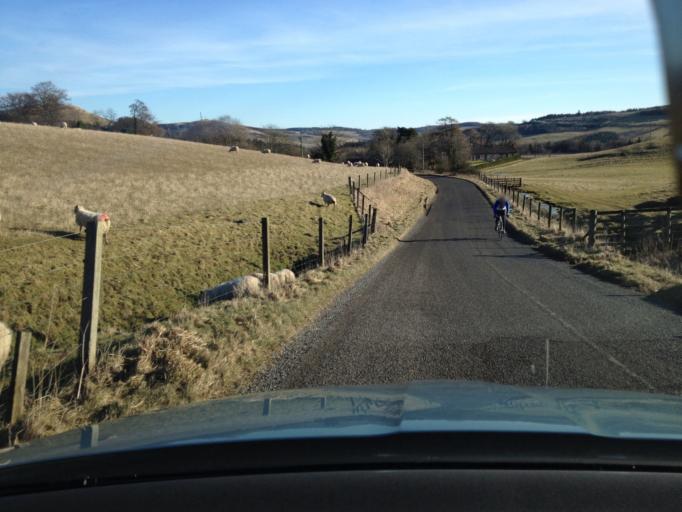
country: GB
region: Scotland
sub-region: Perth and Kinross
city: Bridge of Earn
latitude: 56.3008
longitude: -3.3923
